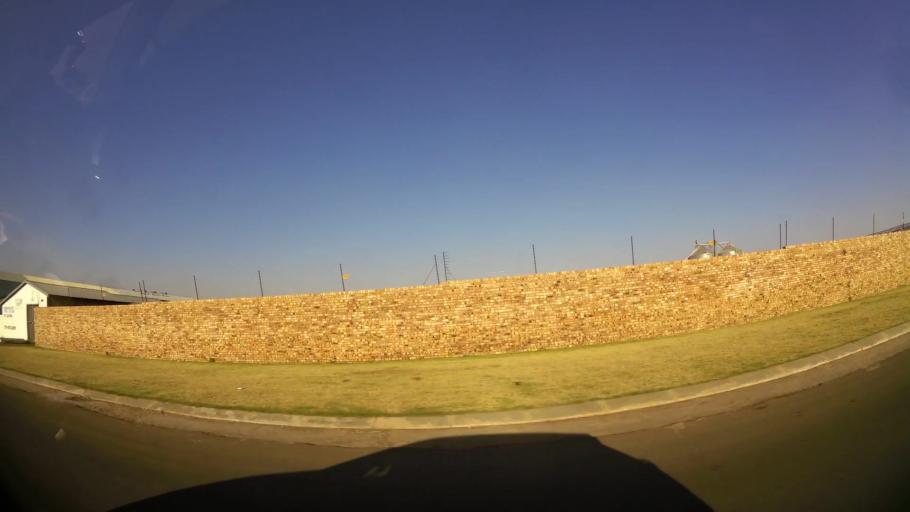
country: ZA
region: Gauteng
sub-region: West Rand District Municipality
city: Randfontein
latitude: -26.1941
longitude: 27.6859
